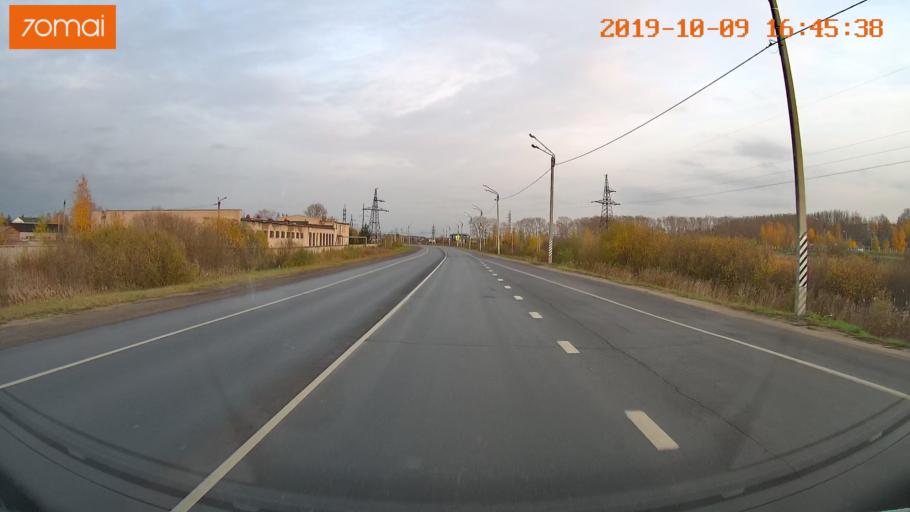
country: RU
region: Kostroma
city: Volgorechensk
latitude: 57.4456
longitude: 41.1580
